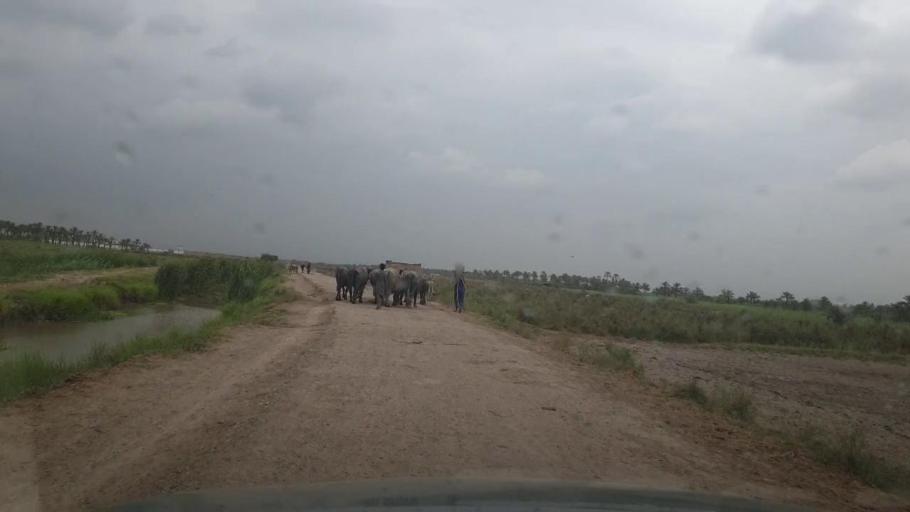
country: PK
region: Sindh
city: Khairpur
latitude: 27.5542
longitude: 68.6927
